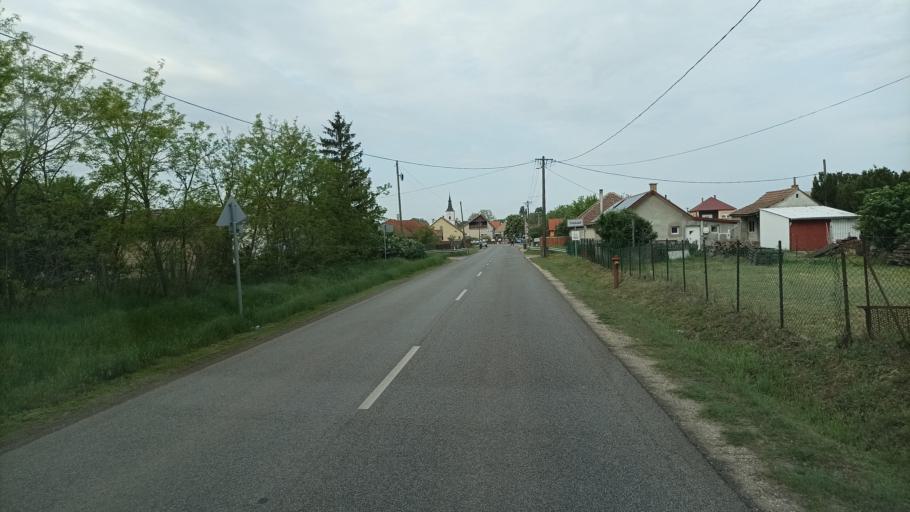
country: HU
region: Pest
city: Monor
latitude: 47.3261
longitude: 19.4061
